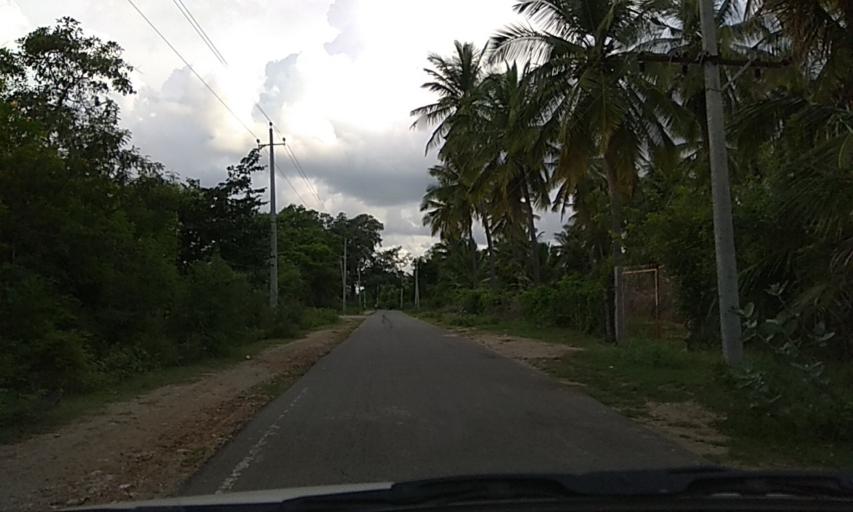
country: IN
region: Karnataka
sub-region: Chamrajnagar
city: Gundlupet
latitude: 11.8783
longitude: 76.7472
